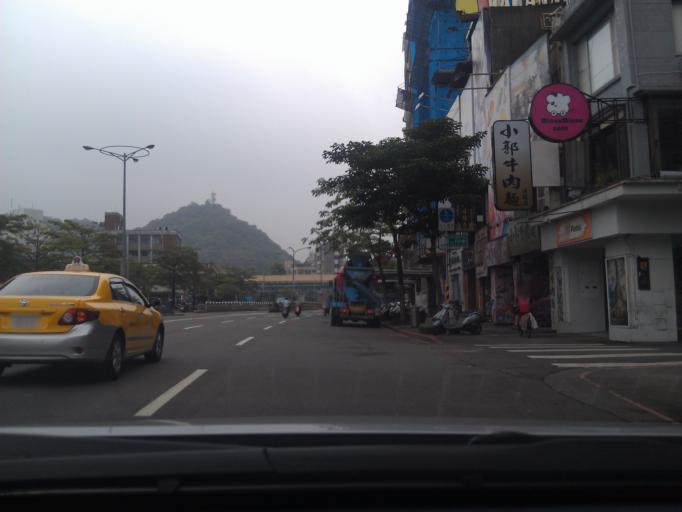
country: TW
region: Taipei
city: Taipei
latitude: 25.0132
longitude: 121.5359
